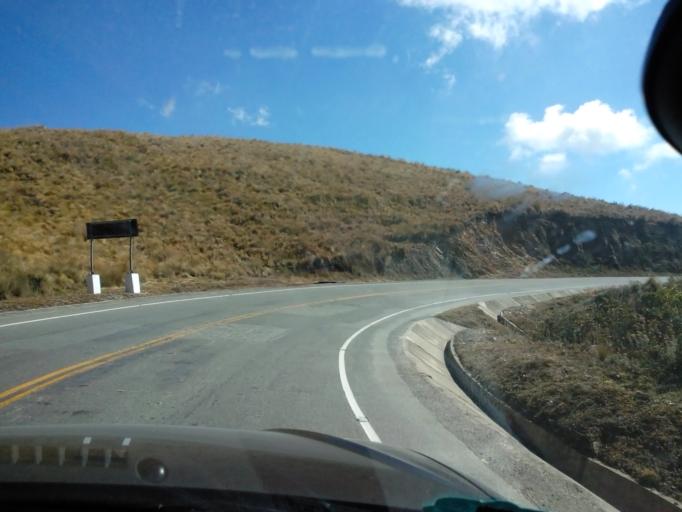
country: PE
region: Apurimac
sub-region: Provincia de Abancay
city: Cachora
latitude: -13.5759
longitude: -72.8197
